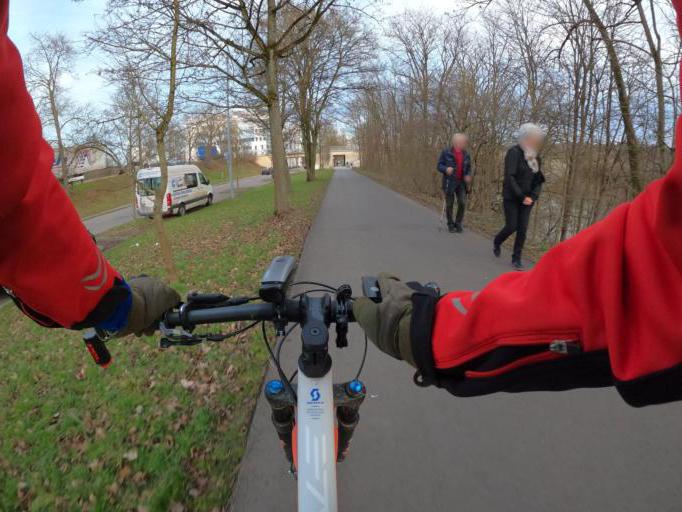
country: DE
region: Baden-Wuerttemberg
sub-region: Regierungsbezirk Stuttgart
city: Denkendorf
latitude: 48.7225
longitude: 9.3417
